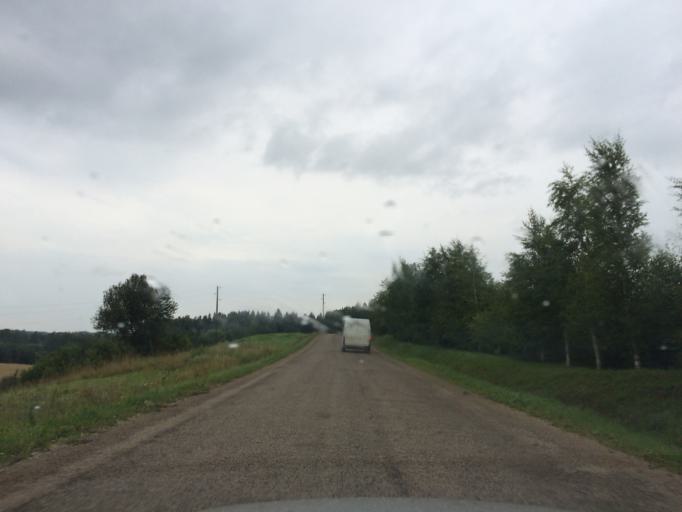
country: LV
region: Rezekne
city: Rezekne
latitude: 56.5643
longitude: 27.4519
